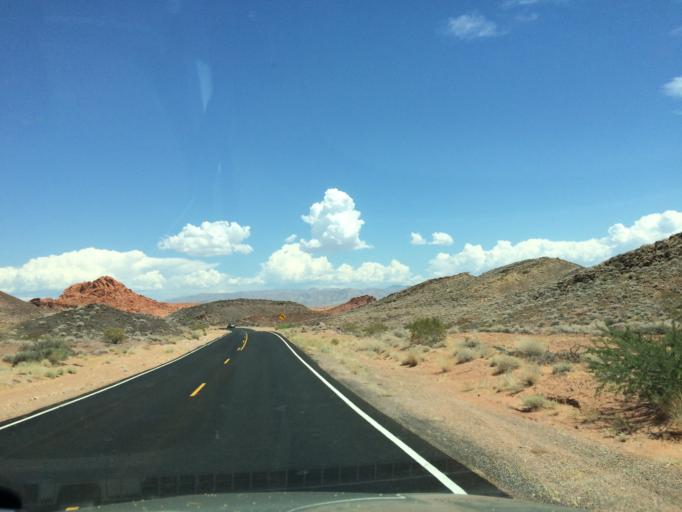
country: US
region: Nevada
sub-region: Clark County
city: Moapa Valley
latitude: 36.4266
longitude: -114.4760
